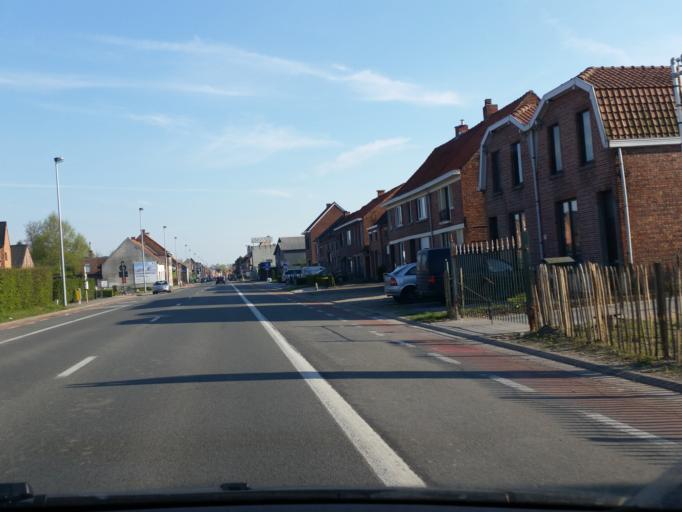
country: BE
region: Flanders
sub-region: Provincie Oost-Vlaanderen
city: Stekene
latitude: 51.2135
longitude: 4.0709
